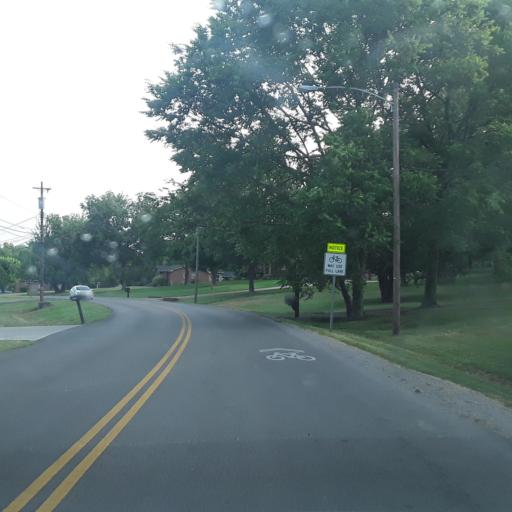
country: US
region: Tennessee
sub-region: Williamson County
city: Brentwood Estates
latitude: 36.0521
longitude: -86.7241
